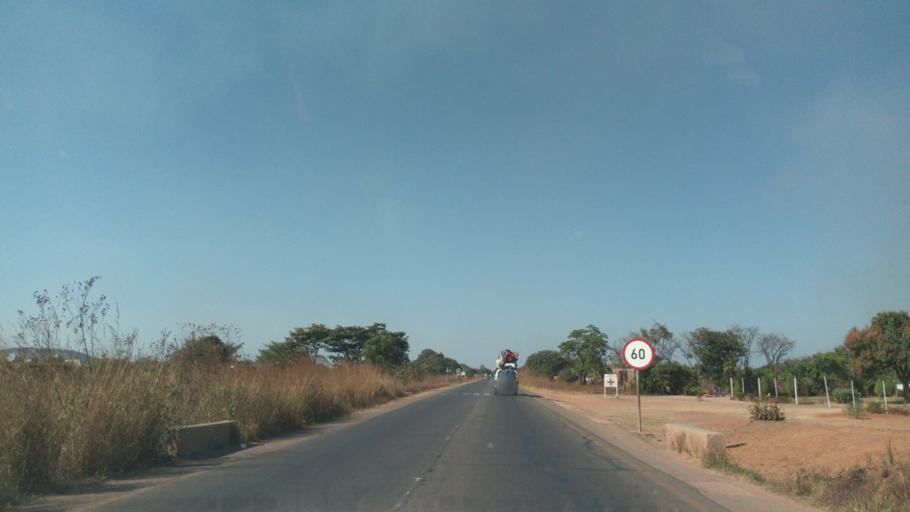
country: CD
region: Katanga
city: Lubumbashi
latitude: -11.5606
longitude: 27.5695
